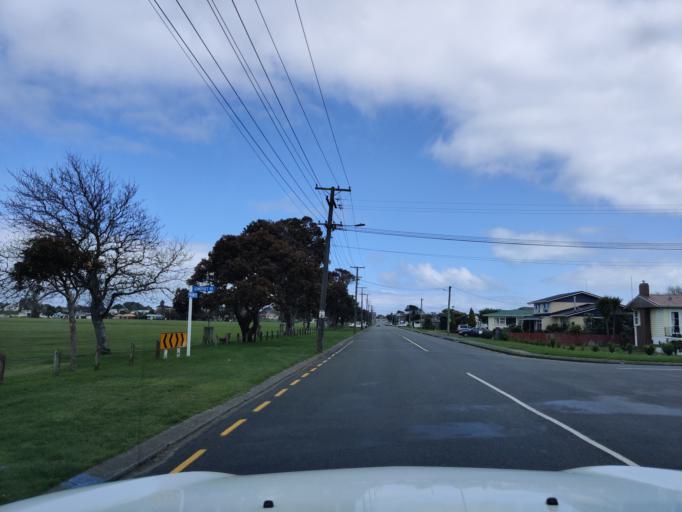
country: NZ
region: Manawatu-Wanganui
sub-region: Wanganui District
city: Wanganui
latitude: -39.9281
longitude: 175.0285
